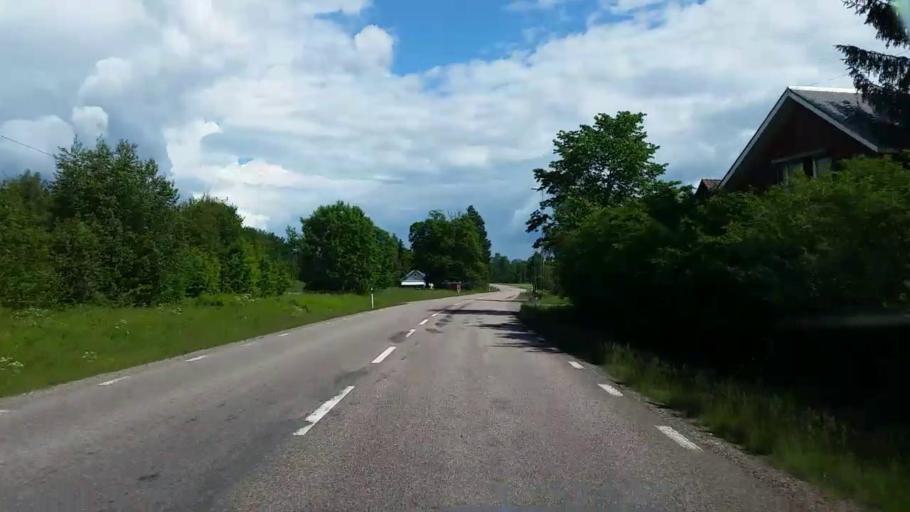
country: SE
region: Dalarna
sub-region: Avesta Kommun
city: Avesta
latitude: 60.1576
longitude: 16.2566
